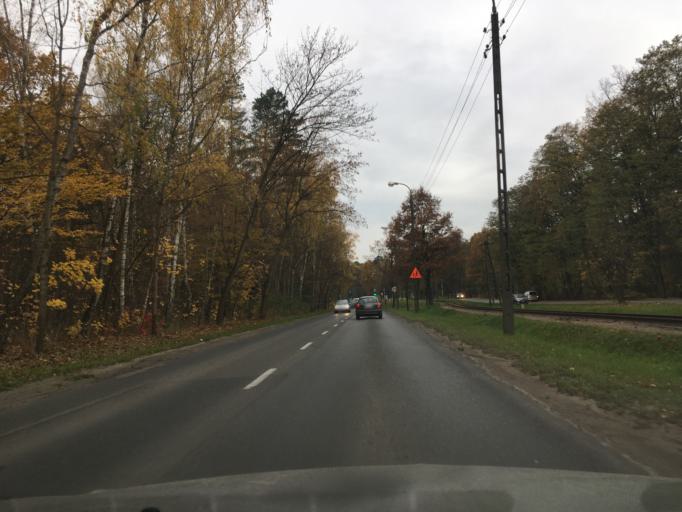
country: PL
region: Masovian Voivodeship
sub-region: Powiat piaseczynski
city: Piaseczno
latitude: 52.0615
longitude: 21.0127
